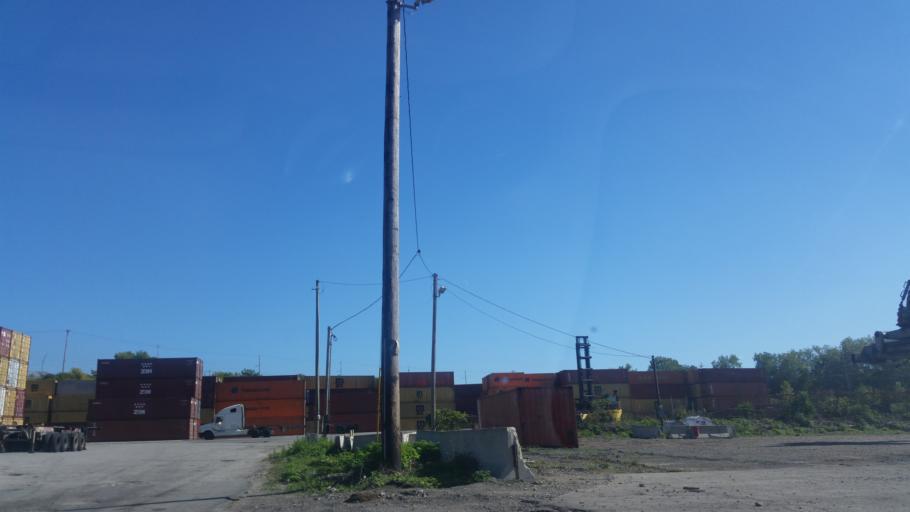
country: US
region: Ohio
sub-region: Cuyahoga County
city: Cleveland
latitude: 41.4866
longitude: -81.6701
